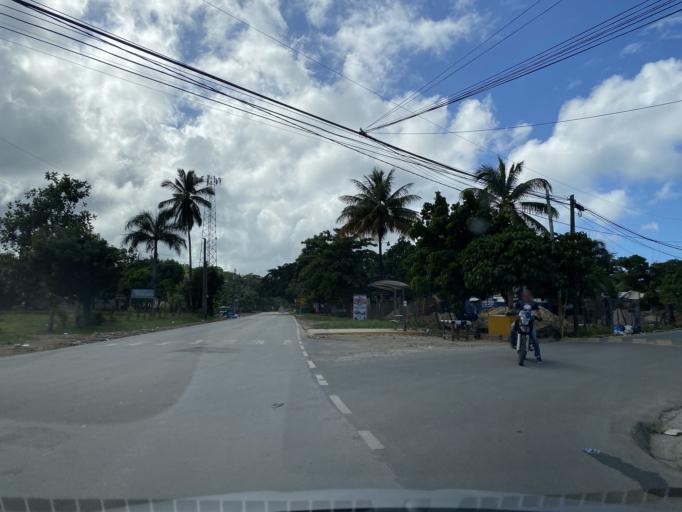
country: DO
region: Samana
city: Las Terrenas
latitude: 19.3066
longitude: -69.5399
